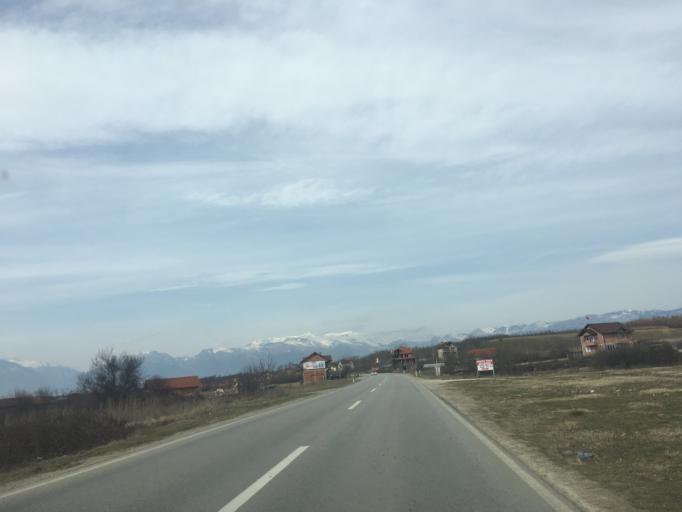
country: XK
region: Pec
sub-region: Komuna e Pejes
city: Kosuriq
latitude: 42.6135
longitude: 20.5006
